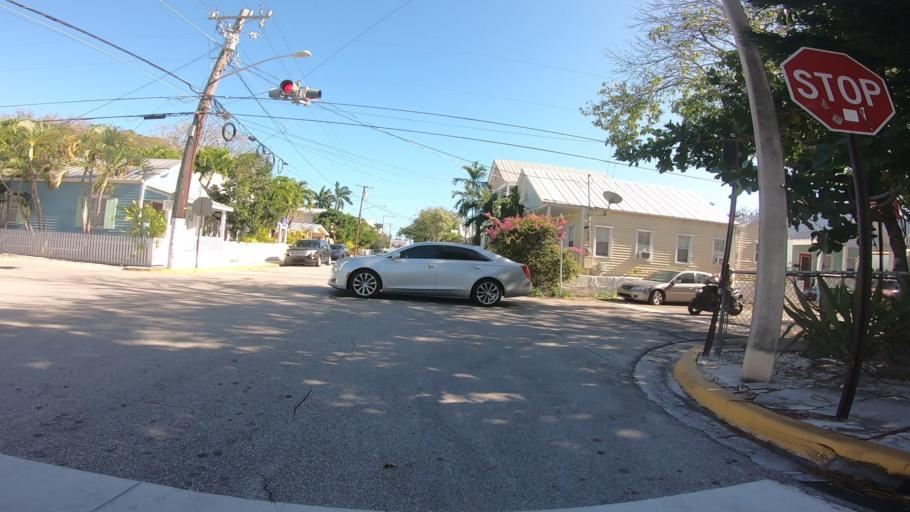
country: US
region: Florida
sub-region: Monroe County
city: Key West
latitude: 24.5507
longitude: -81.8022
